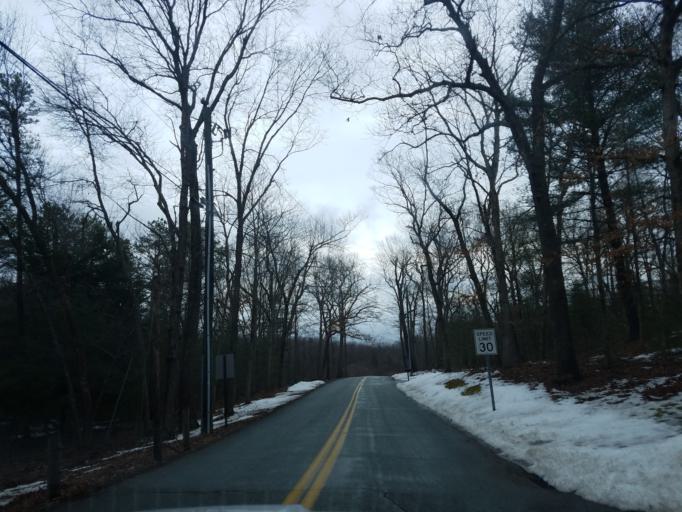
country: US
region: Connecticut
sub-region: Hartford County
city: Glastonbury Center
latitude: 41.6729
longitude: -72.5566
